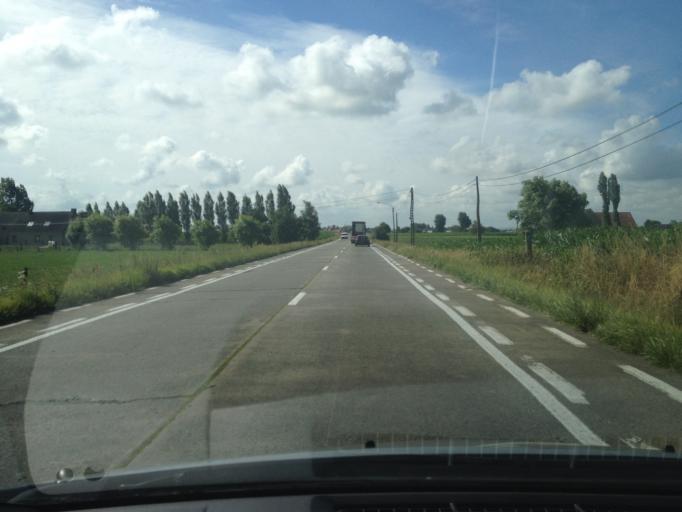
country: BE
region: Flanders
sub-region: Provincie West-Vlaanderen
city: Alveringem
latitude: 50.9885
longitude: 2.6886
